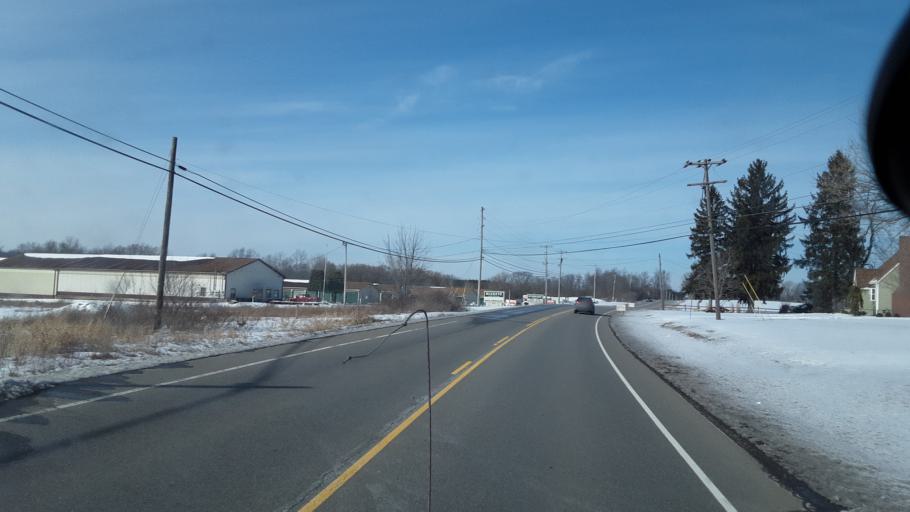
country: US
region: Ohio
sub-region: Mahoning County
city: Canfield
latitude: 40.9915
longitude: -80.7607
